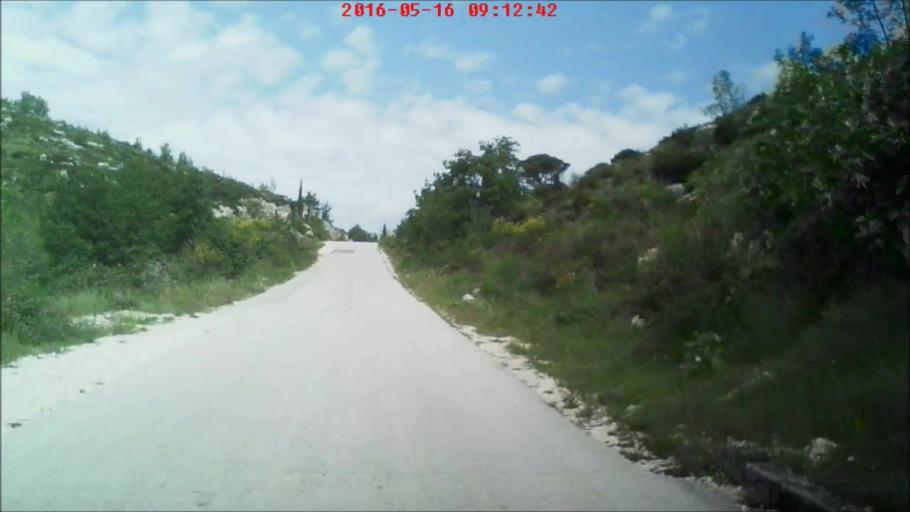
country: HR
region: Dubrovacko-Neretvanska
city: Podgora
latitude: 42.8290
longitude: 17.8486
